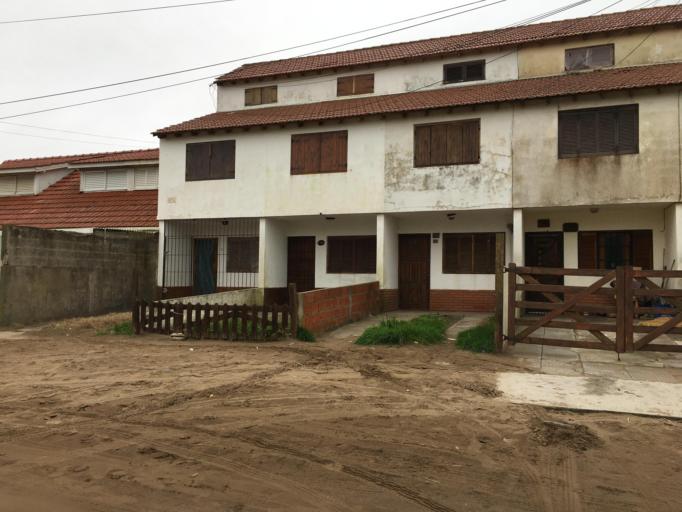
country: AR
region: Buenos Aires
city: Mar del Tuyu
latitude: -36.5547
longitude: -56.6891
